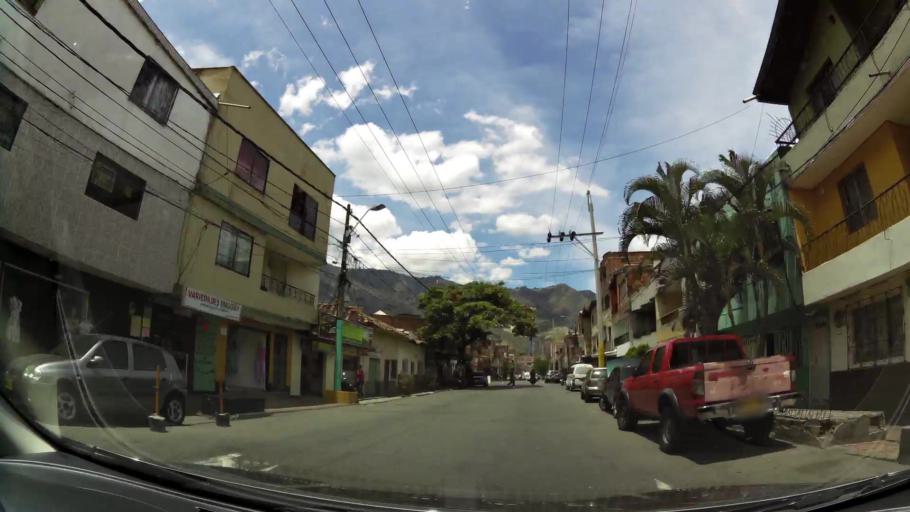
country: CO
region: Antioquia
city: Bello
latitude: 6.3418
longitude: -75.5611
